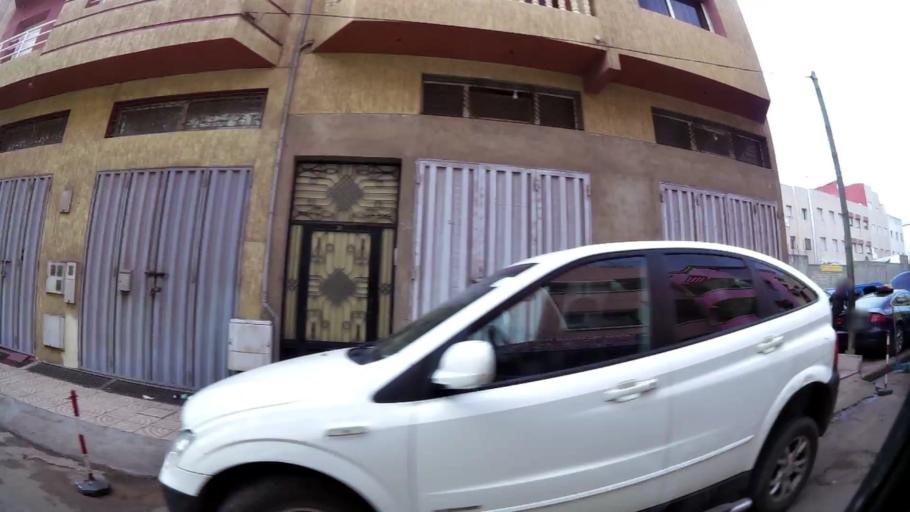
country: MA
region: Grand Casablanca
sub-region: Mohammedia
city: Mohammedia
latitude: 33.6861
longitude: -7.3775
